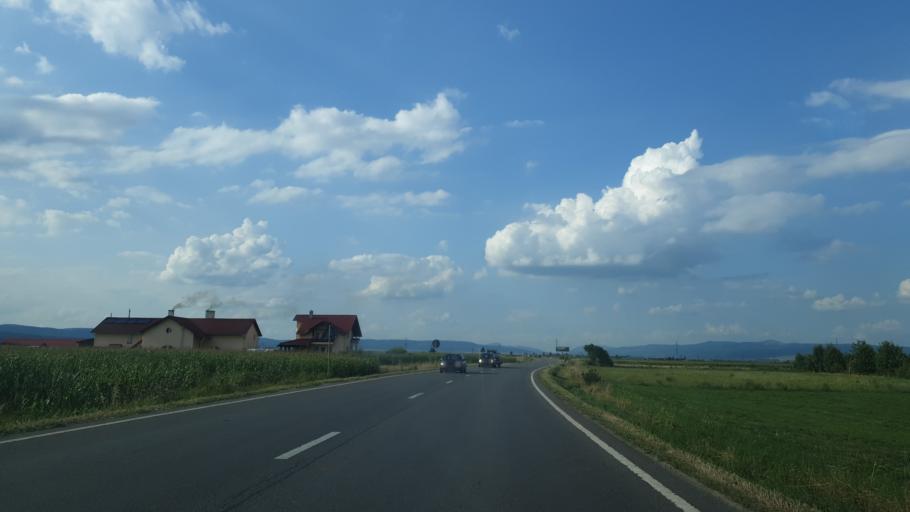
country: RO
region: Covasna
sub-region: Comuna Chichis
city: Chichis
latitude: 45.8164
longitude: 25.7988
